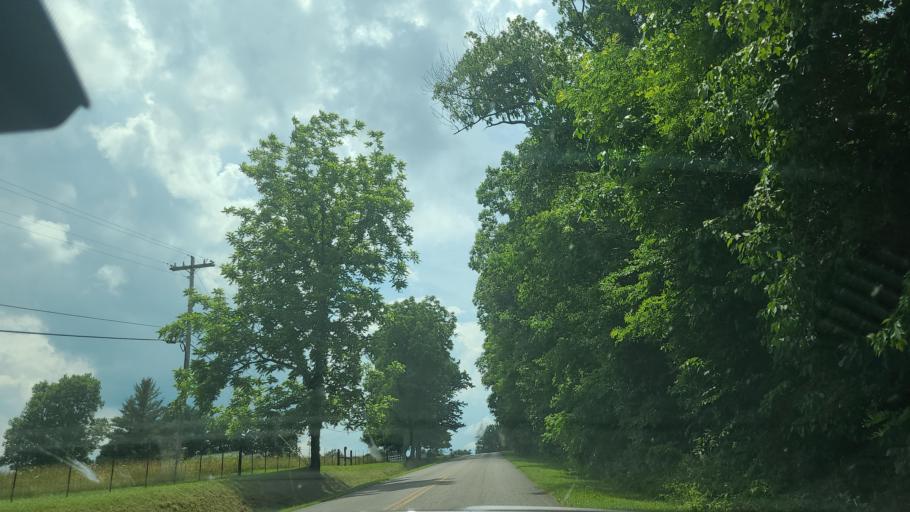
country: US
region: Tennessee
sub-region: Cumberland County
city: Lake Tansi
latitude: 35.8065
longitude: -85.0252
